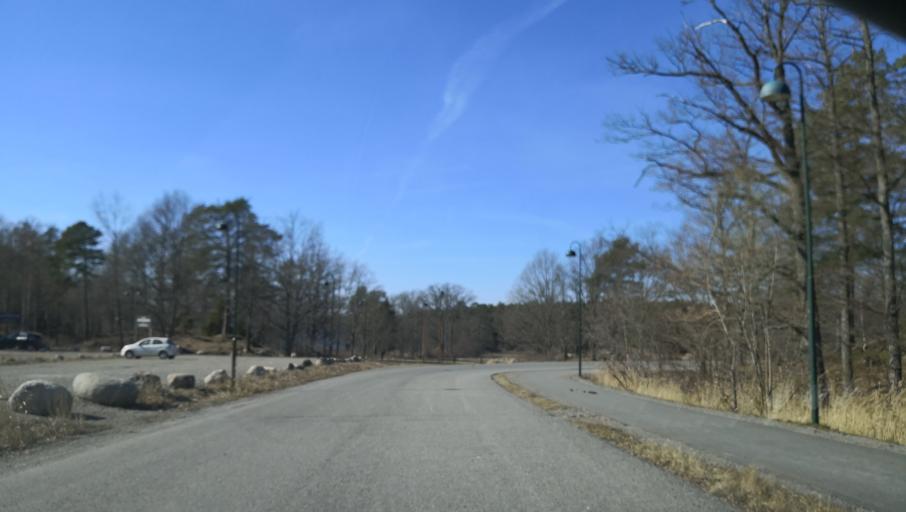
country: SE
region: Stockholm
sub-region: Varmdo Kommun
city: Gustavsberg
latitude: 59.3077
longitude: 18.3554
